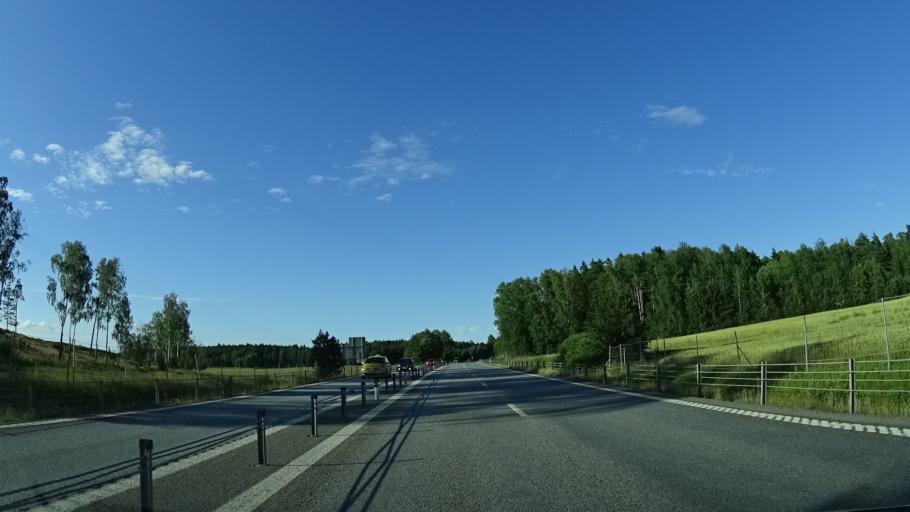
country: SE
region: Stockholm
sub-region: Osterakers Kommun
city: Akersberga
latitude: 59.5701
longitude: 18.2346
